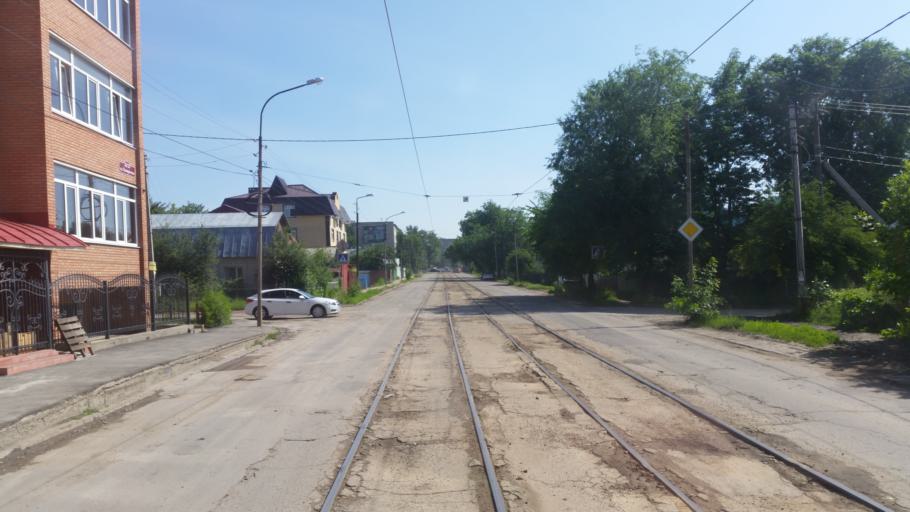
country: RU
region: Ulyanovsk
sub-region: Ulyanovskiy Rayon
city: Ulyanovsk
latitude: 54.3434
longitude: 48.3834
